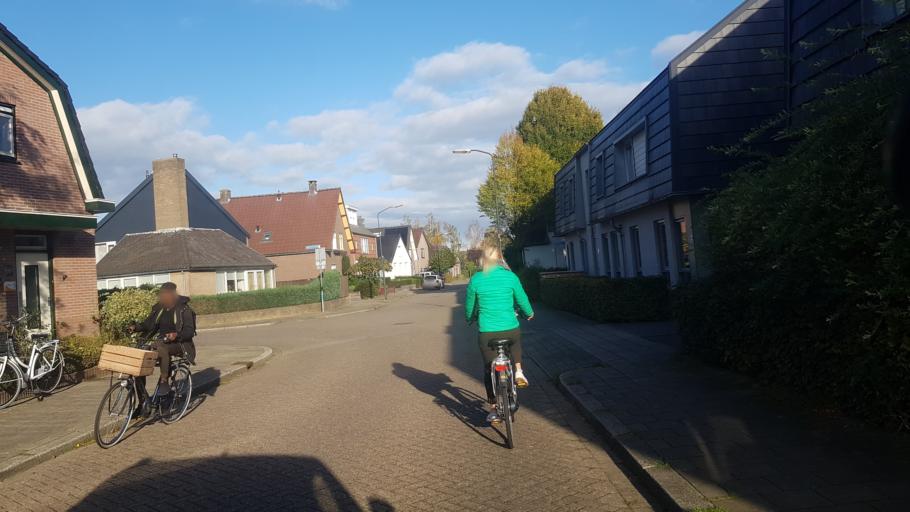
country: NL
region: Gelderland
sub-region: Gemeente Apeldoorn
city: Apeldoorn
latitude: 52.2121
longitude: 5.9459
